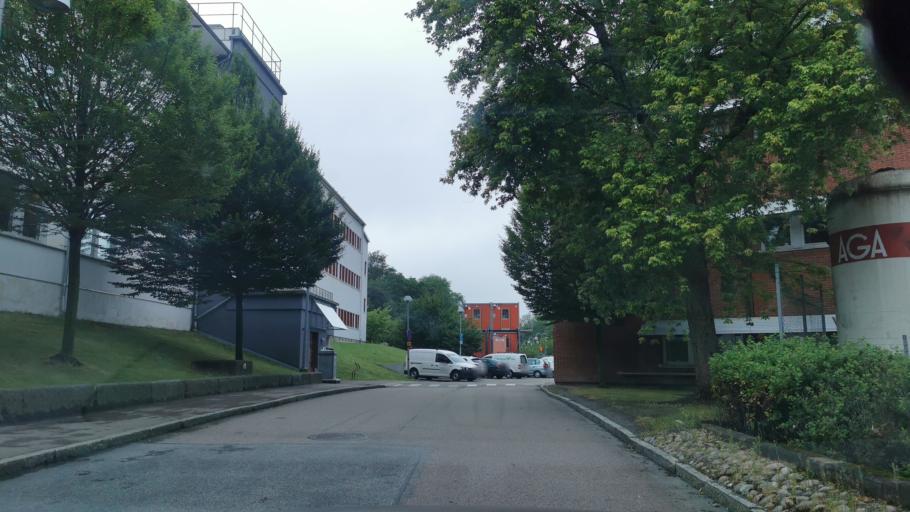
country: SE
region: Vaestra Goetaland
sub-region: Goteborg
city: Goeteborg
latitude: 57.6808
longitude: 11.9635
